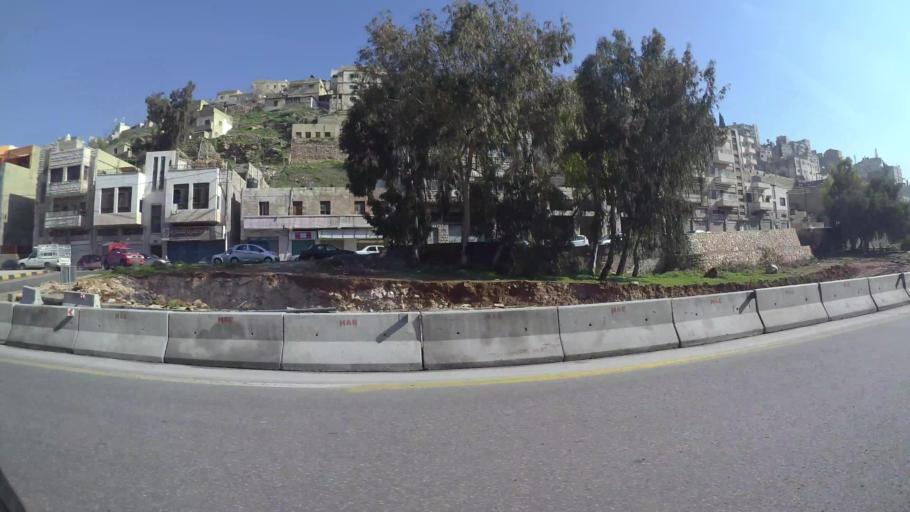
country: JO
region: Amman
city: Amman
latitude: 31.9462
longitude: 35.9185
